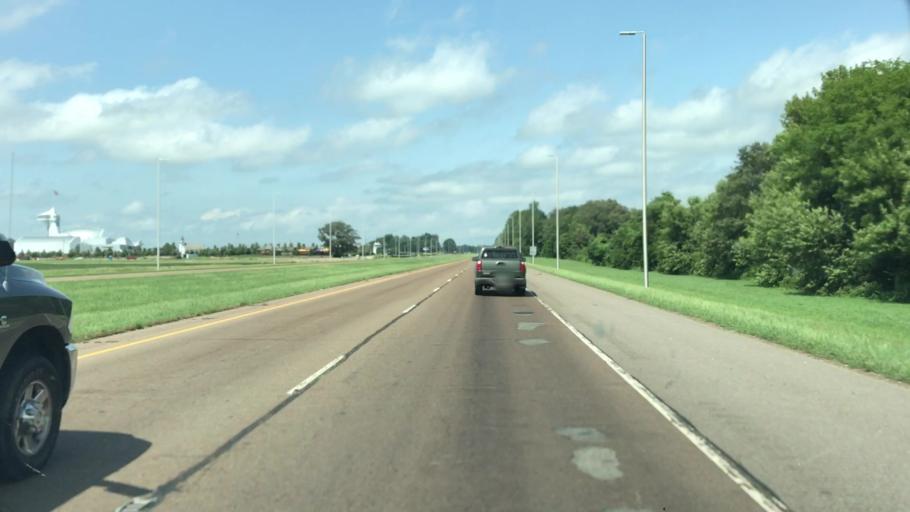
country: US
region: Tennessee
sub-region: Obion County
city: Union City
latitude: 36.4311
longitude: -89.0672
